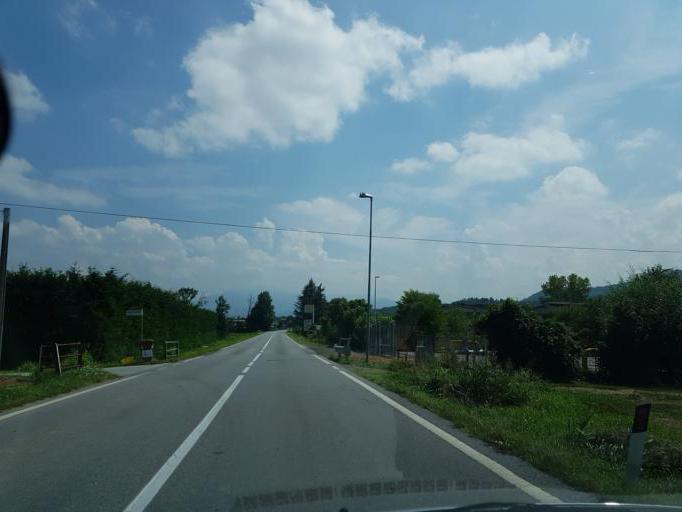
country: IT
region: Piedmont
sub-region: Provincia di Cuneo
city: San Rocco
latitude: 44.3956
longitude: 7.4541
